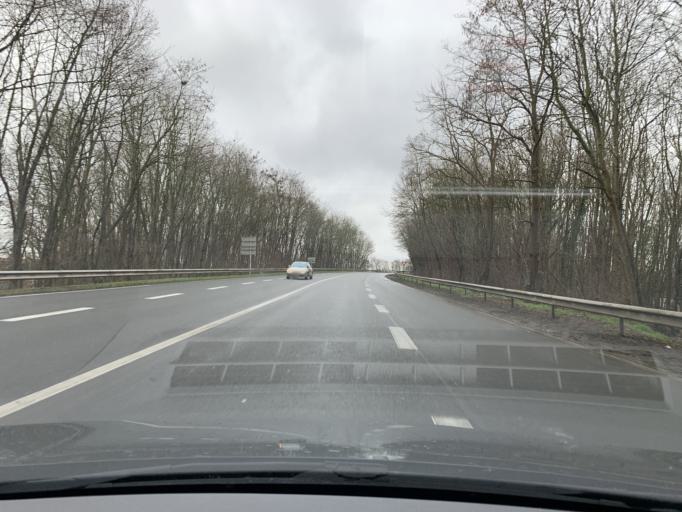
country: FR
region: Nord-Pas-de-Calais
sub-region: Departement du Nord
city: Dechy
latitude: 50.3568
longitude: 3.1220
